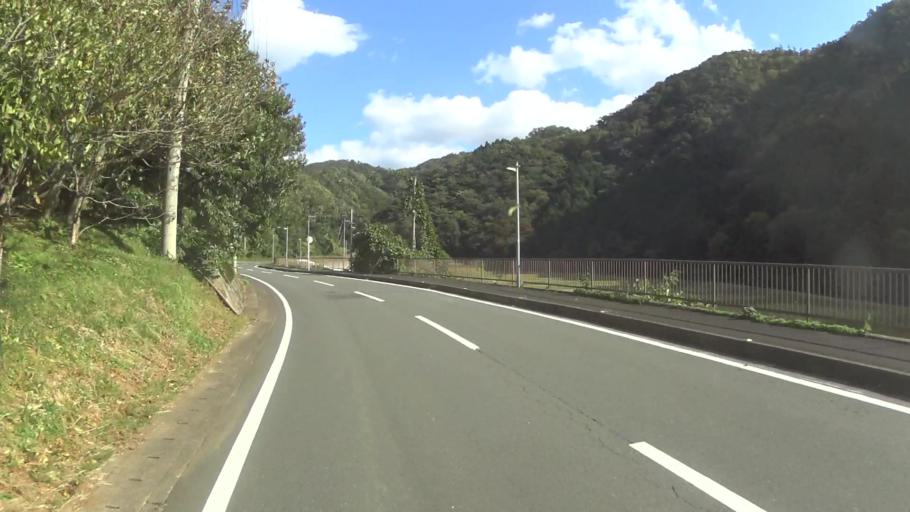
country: JP
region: Kyoto
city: Maizuru
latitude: 35.5210
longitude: 135.3600
